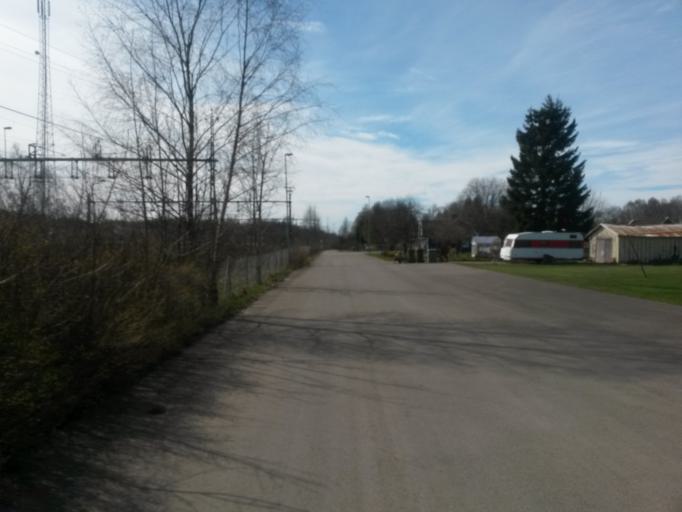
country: SE
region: Vaestra Goetaland
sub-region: Falkopings Kommun
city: Floby
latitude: 58.1391
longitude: 13.3330
